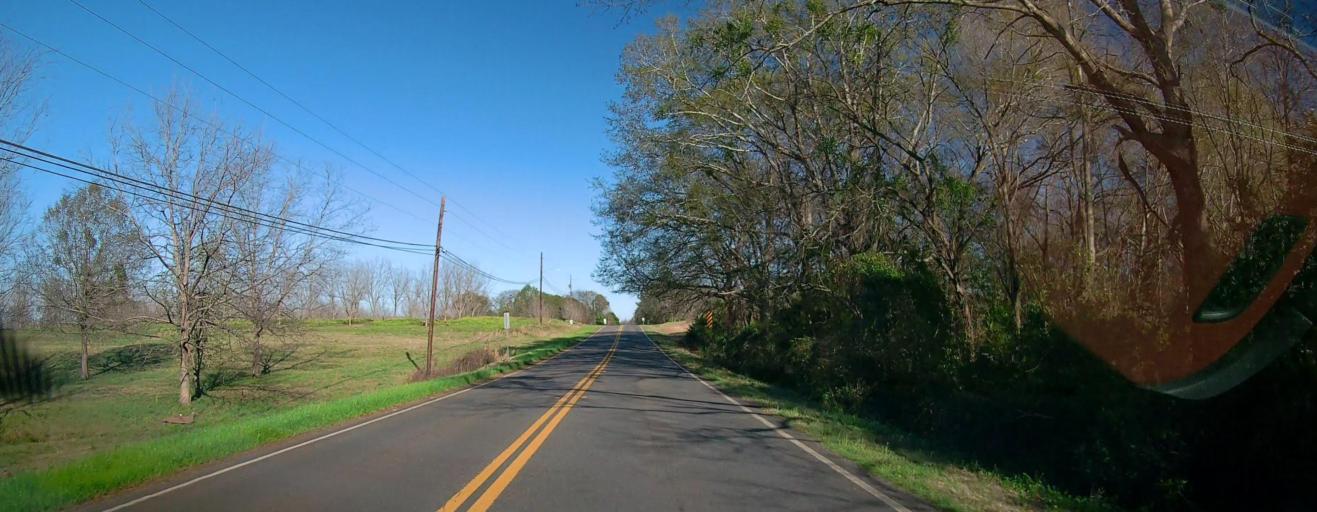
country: US
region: Georgia
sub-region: Macon County
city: Marshallville
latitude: 32.4562
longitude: -83.9322
